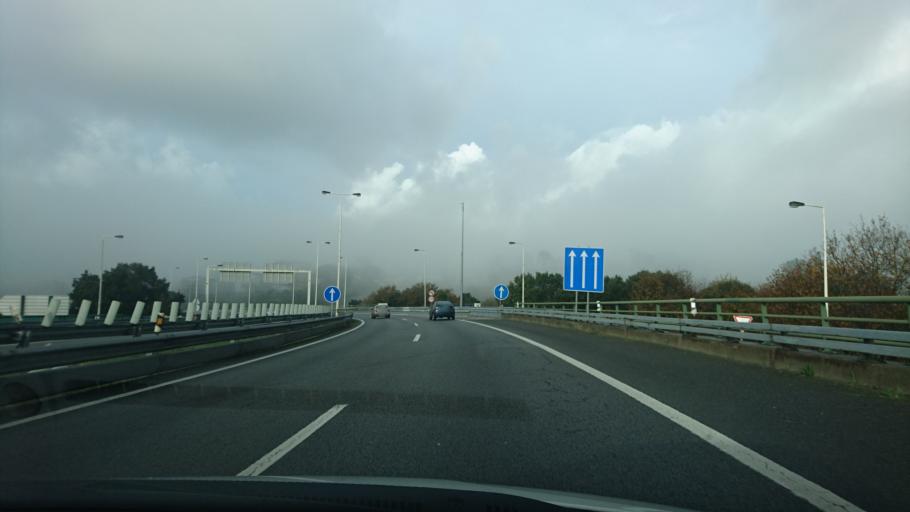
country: PT
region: Porto
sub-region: Gondomar
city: Rio Tinto
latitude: 41.1586
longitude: -8.5622
